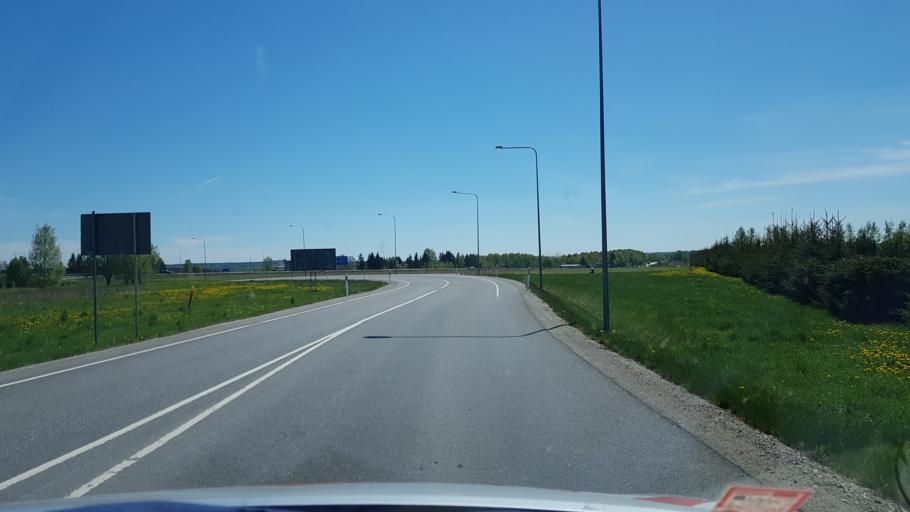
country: EE
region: Tartu
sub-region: UElenurme vald
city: Ulenurme
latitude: 58.3132
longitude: 26.7151
